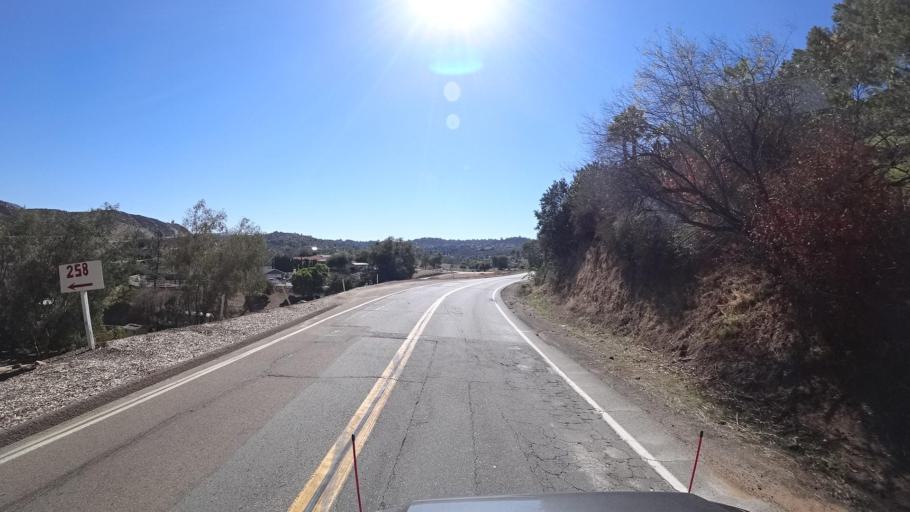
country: US
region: California
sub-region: San Diego County
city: Harbison Canyon
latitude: 32.8468
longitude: -116.8102
